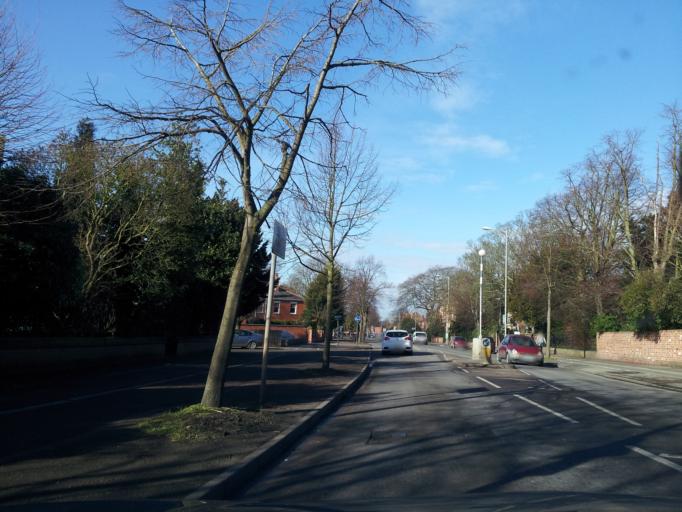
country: GB
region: England
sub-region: Nottinghamshire
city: Newark on Trent
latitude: 53.0702
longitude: -0.8002
